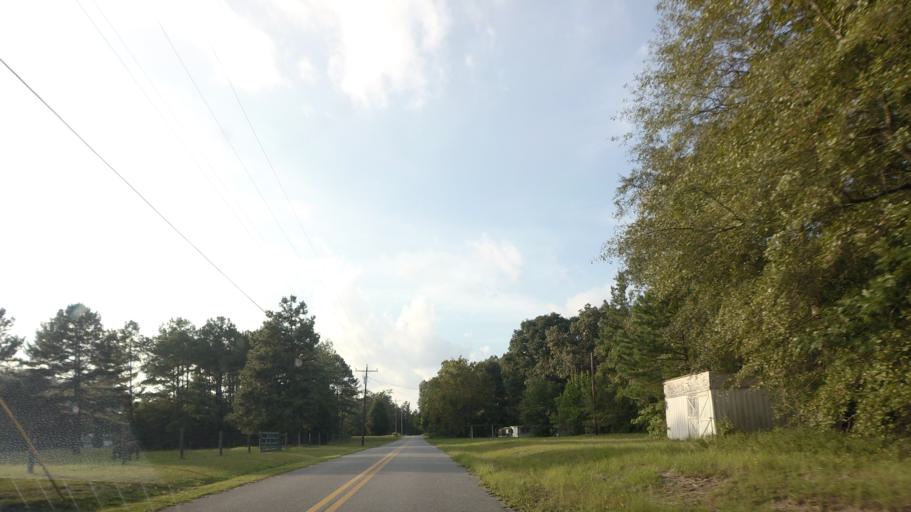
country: US
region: Georgia
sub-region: Wilkinson County
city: Gordon
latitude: 32.8324
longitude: -83.3926
